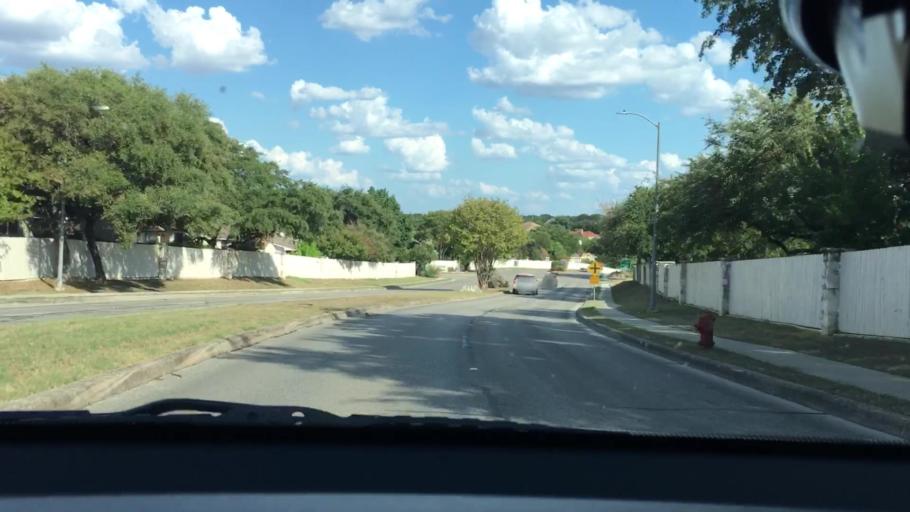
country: US
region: Texas
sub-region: Bexar County
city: Selma
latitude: 29.5672
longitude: -98.3143
